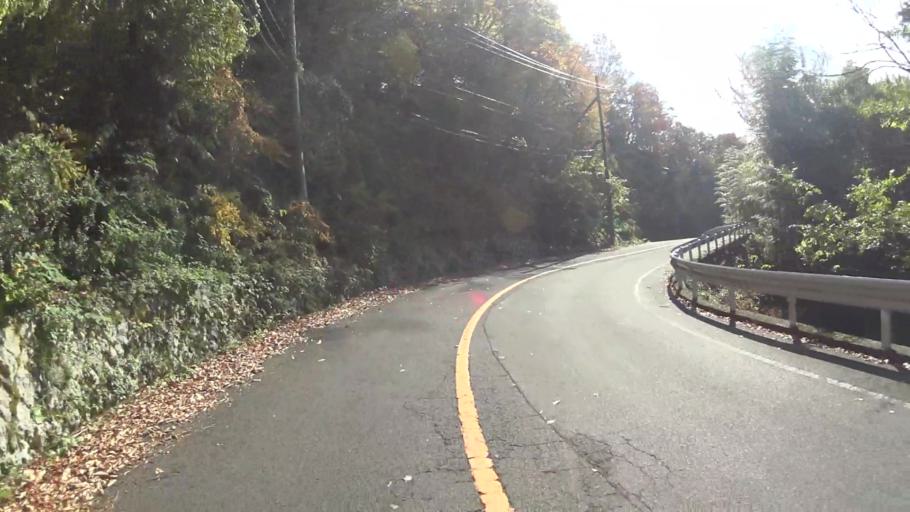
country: JP
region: Kyoto
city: Maizuru
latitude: 35.4620
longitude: 135.3534
